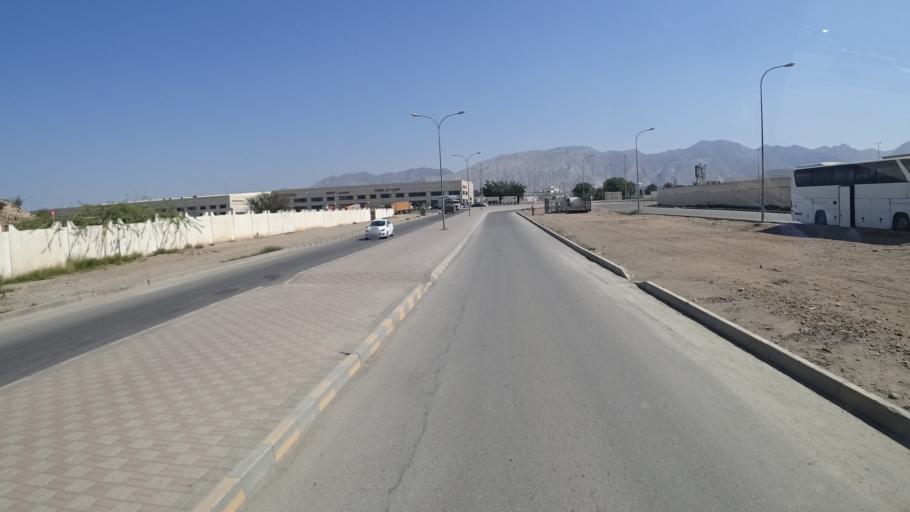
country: OM
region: Muhafazat Masqat
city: Bawshar
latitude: 23.5718
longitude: 58.3791
